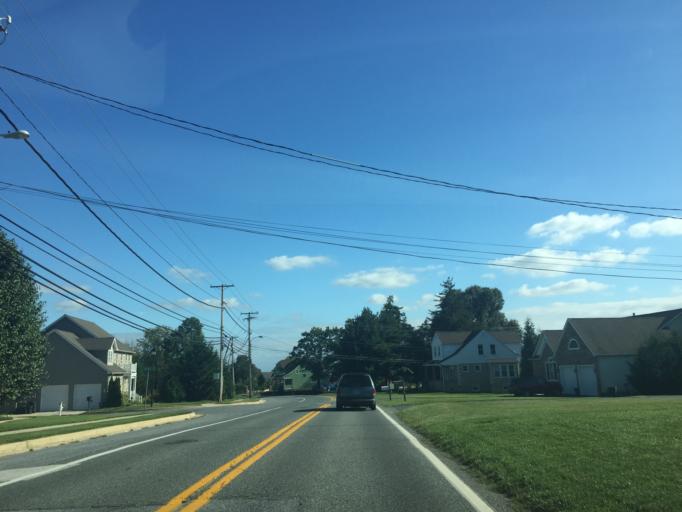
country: US
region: Maryland
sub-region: Baltimore County
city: Overlea
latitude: 39.3670
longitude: -76.4964
